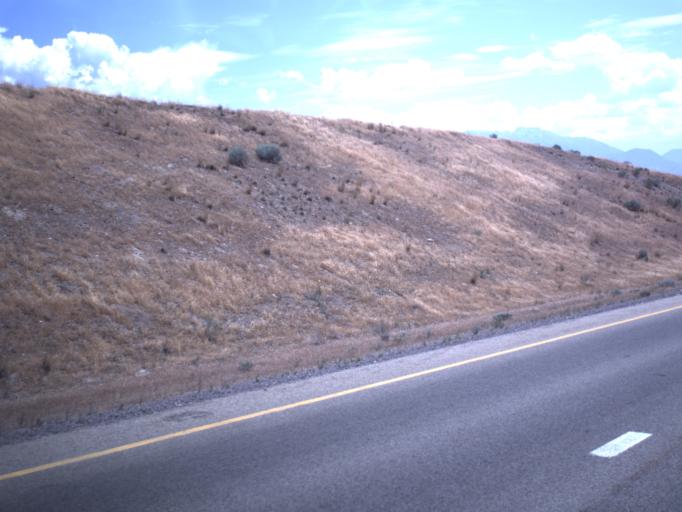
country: US
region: Utah
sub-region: Salt Lake County
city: Bluffdale
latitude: 40.4634
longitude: -111.9554
